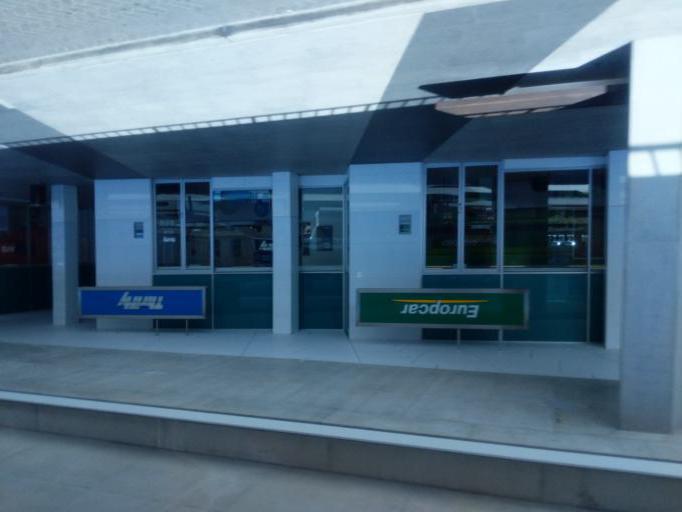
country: AU
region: Australian Capital Territory
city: Forrest
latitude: -35.3080
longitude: 149.1896
